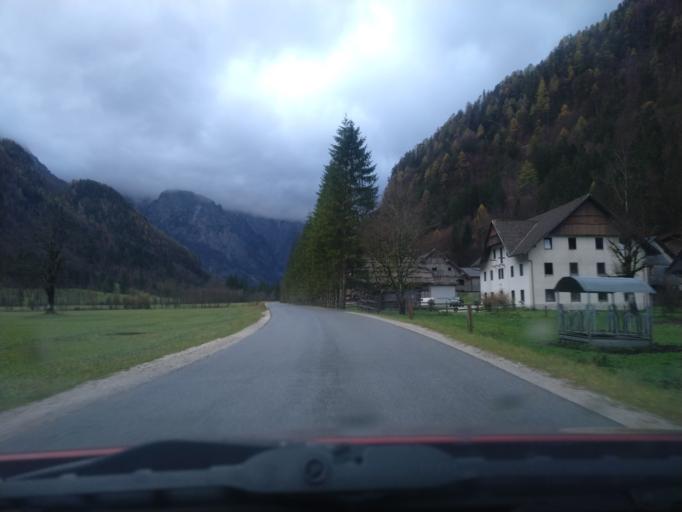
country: SI
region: Solcava
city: Solcava
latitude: 46.4146
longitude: 14.6395
